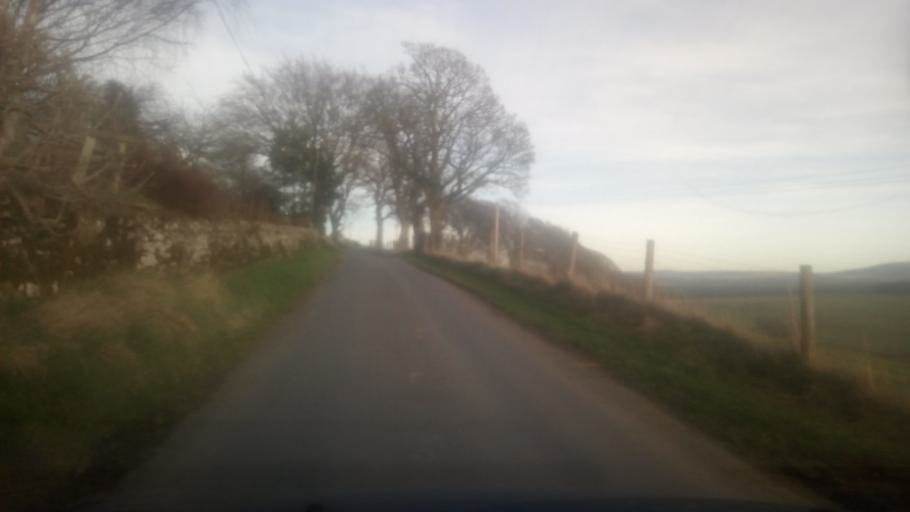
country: GB
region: Scotland
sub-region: The Scottish Borders
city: Jedburgh
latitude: 55.3881
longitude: -2.5885
